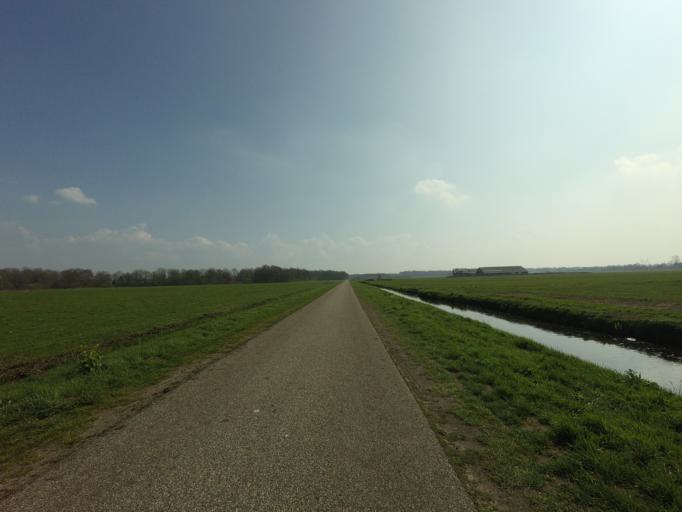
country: NL
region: North Holland
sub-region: Gemeente Bussum
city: Bussum
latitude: 52.2719
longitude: 5.1268
